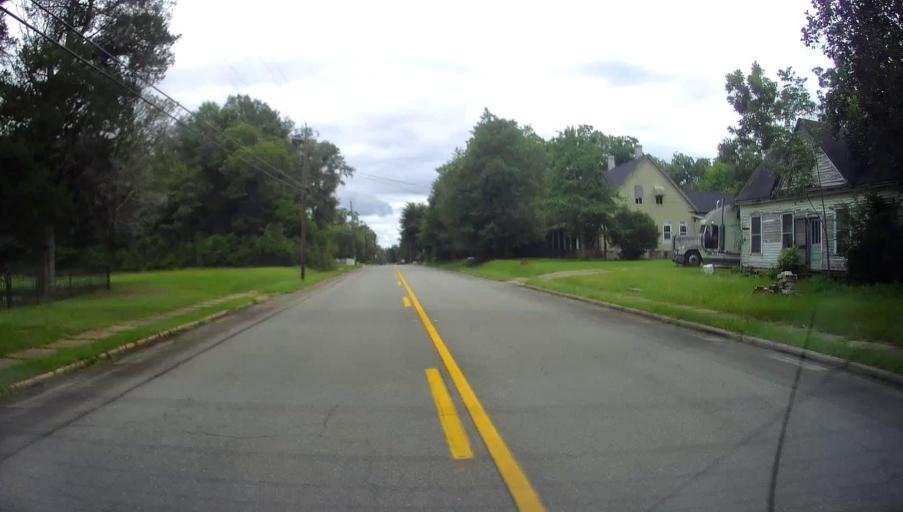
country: US
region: Georgia
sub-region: Twiggs County
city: Jeffersonville
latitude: 32.6847
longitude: -83.3393
